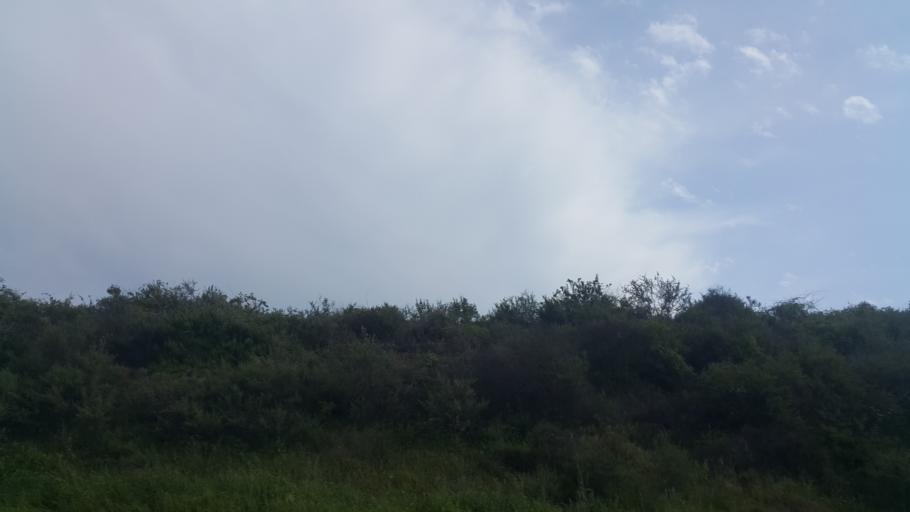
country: TR
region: Mersin
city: Tarsus
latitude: 36.9522
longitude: 34.8211
